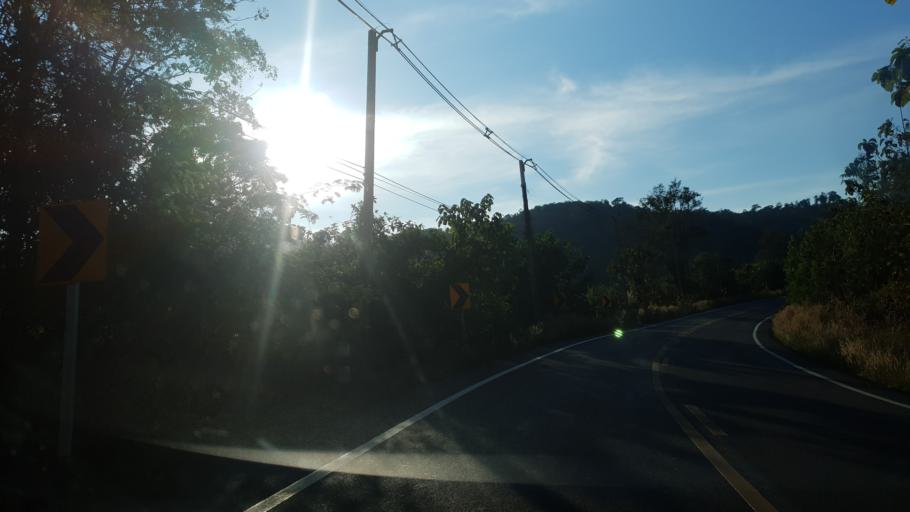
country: TH
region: Loei
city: Dan Sai
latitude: 17.2241
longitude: 101.0676
